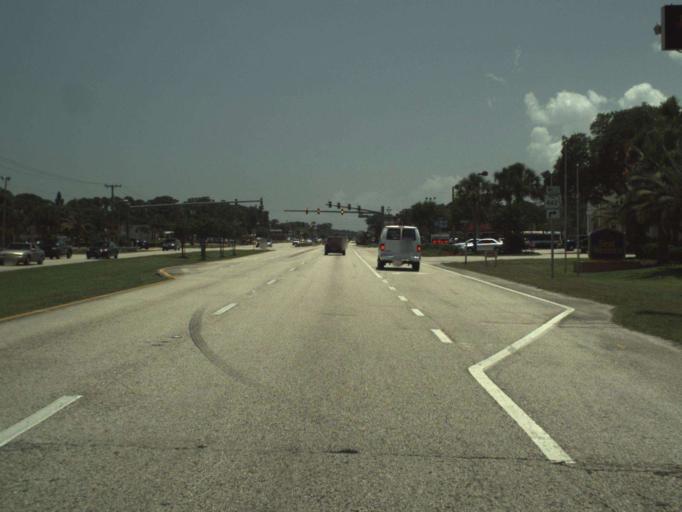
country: US
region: Florida
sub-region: Volusia County
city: Edgewater
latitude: 28.9741
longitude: -80.8969
